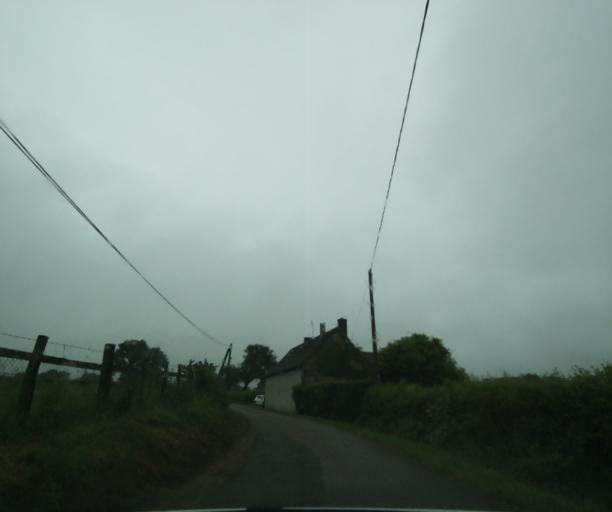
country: FR
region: Bourgogne
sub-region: Departement de Saone-et-Loire
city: Paray-le-Monial
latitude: 46.4121
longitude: 4.1826
